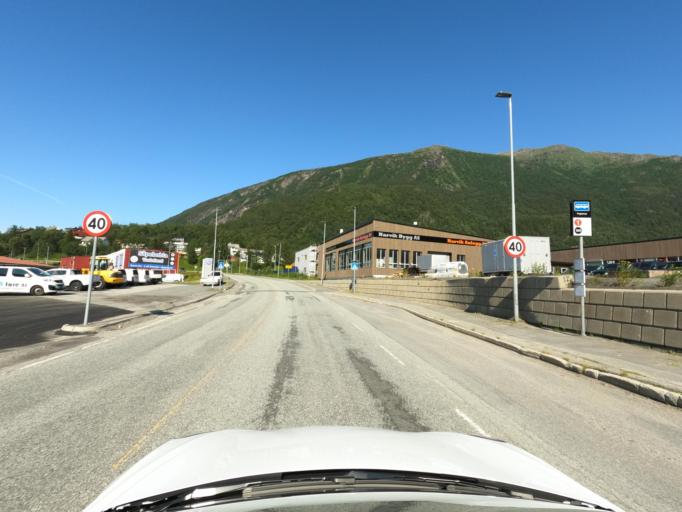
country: NO
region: Nordland
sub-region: Narvik
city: Narvik
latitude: 68.4107
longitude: 17.4299
